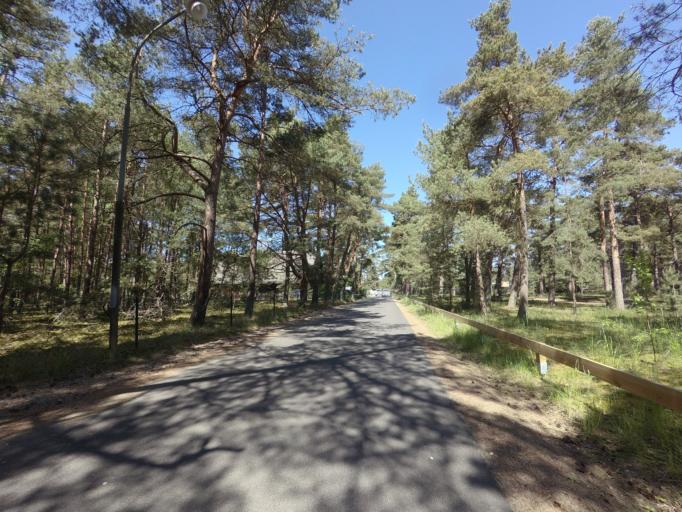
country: SE
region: Skane
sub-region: Vellinge Kommun
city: Hollviken
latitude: 55.4064
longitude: 12.9561
